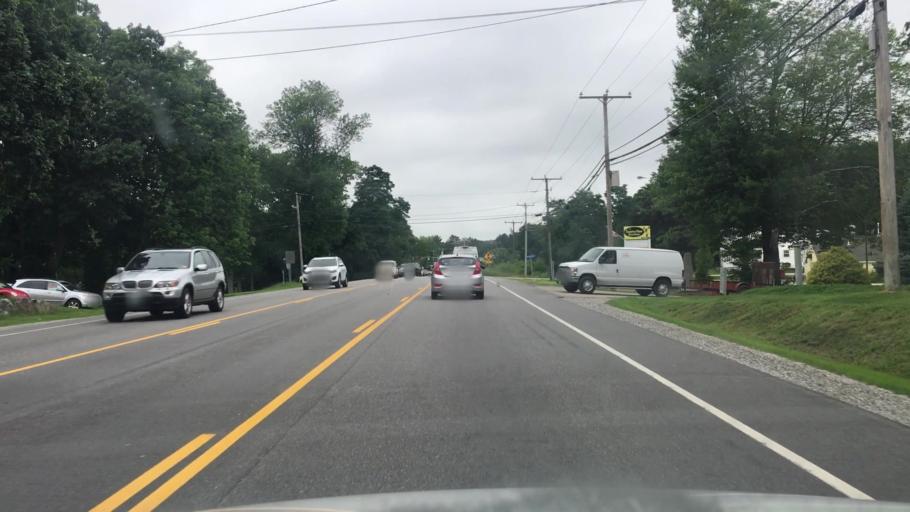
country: US
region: New Hampshire
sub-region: Rockingham County
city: Greenland
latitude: 43.0362
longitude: -70.8451
